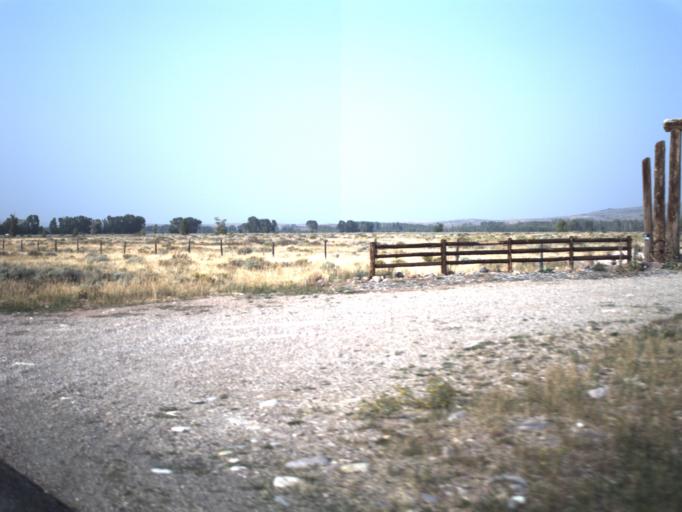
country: US
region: Wyoming
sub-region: Uinta County
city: Evanston
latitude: 40.9898
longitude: -110.8605
